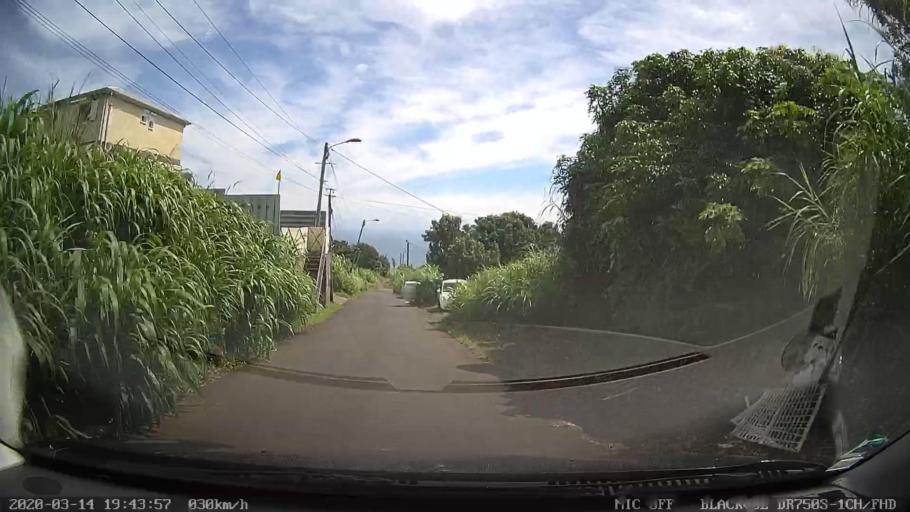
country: RE
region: Reunion
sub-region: Reunion
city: Sainte-Marie
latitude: -20.9466
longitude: 55.5283
